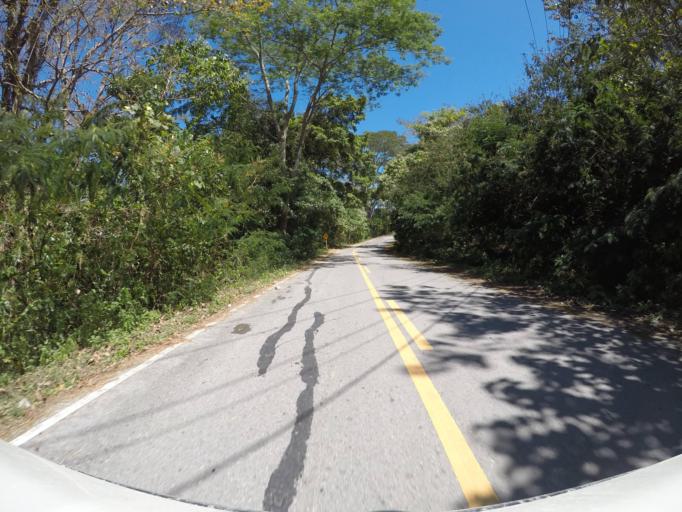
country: TL
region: Manatuto
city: Manatuto
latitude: -8.8191
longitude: 125.9755
